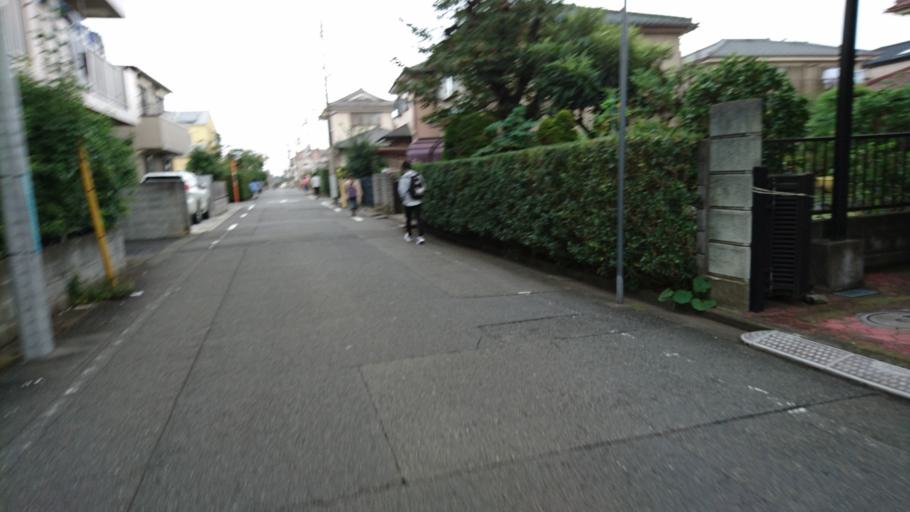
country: JP
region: Tokyo
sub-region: Machida-shi
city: Machida
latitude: 35.5697
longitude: 139.3980
